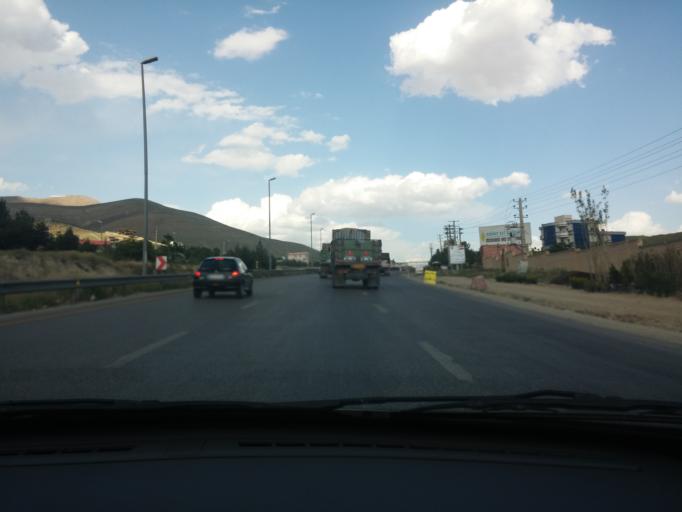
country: IR
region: Tehran
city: Damavand
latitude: 35.7180
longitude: 51.9392
